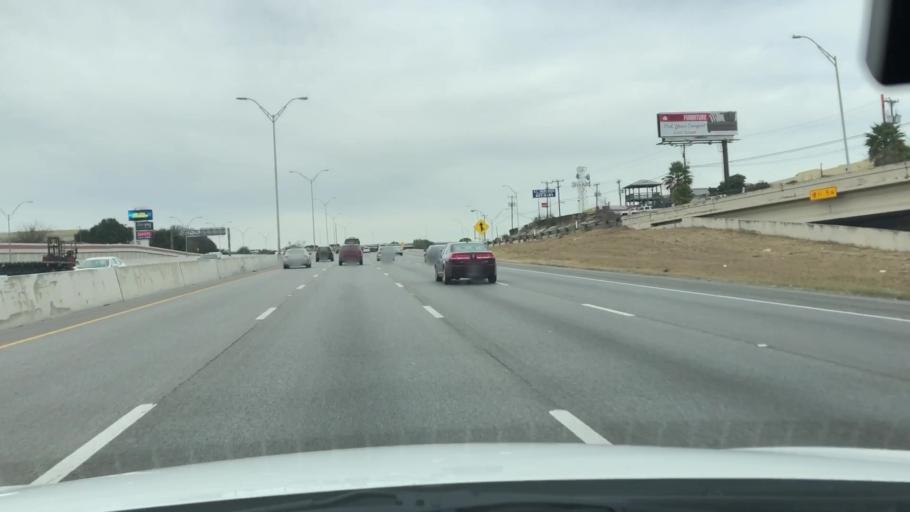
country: US
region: Texas
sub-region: Bexar County
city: Castle Hills
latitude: 29.5346
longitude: -98.4880
